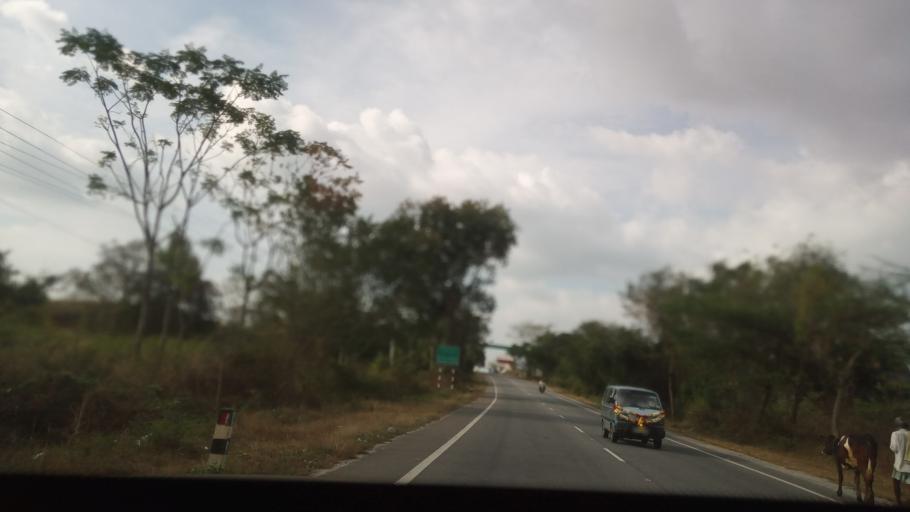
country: IN
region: Karnataka
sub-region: Tumkur
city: Kunigal
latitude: 12.8111
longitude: 77.0361
